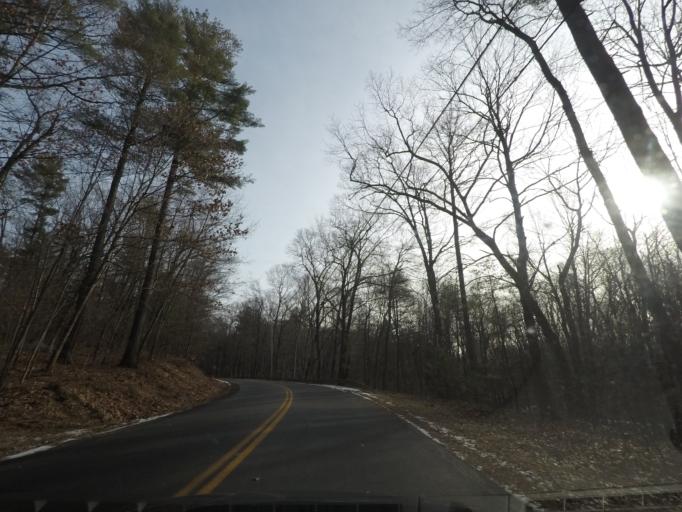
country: US
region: New York
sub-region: Saratoga County
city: Stillwater
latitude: 42.9903
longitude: -73.7241
